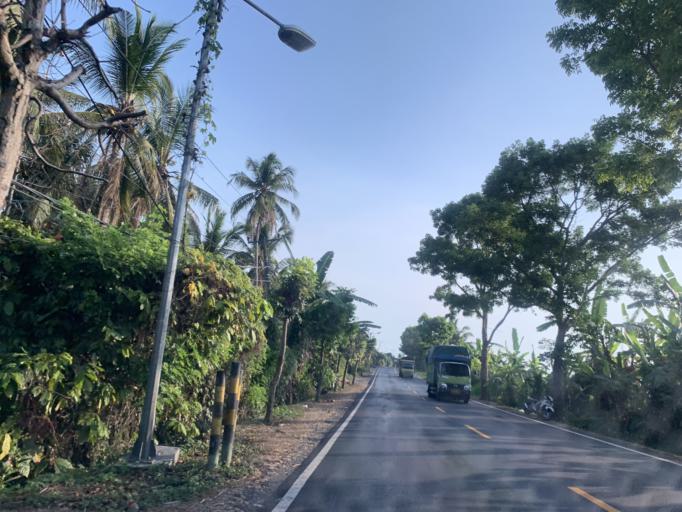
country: ID
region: Bali
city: Banjar Delodrurung
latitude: -8.5114
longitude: 115.0168
